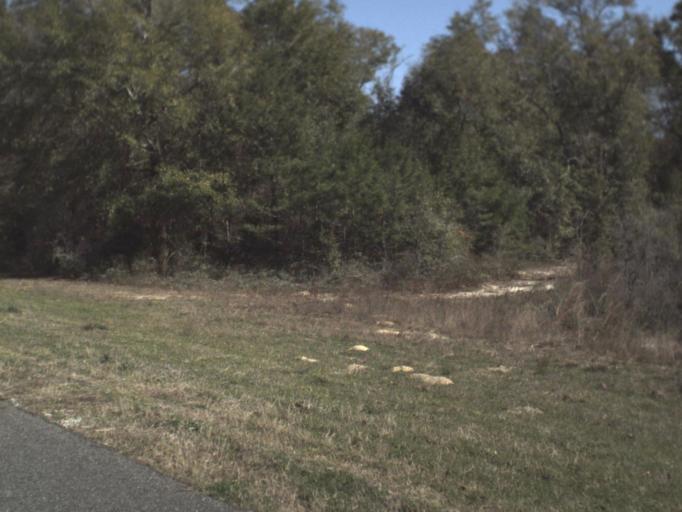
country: US
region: Florida
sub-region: Bay County
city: Youngstown
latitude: 30.4347
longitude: -85.5304
